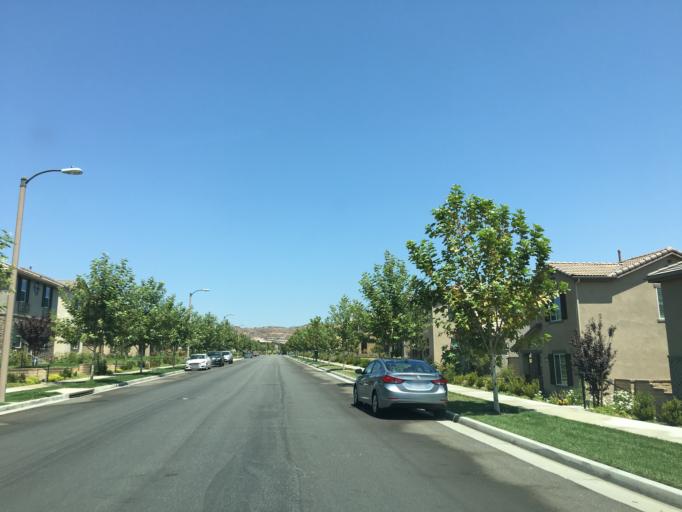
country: US
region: California
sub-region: Los Angeles County
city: Valencia
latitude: 34.4531
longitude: -118.5640
